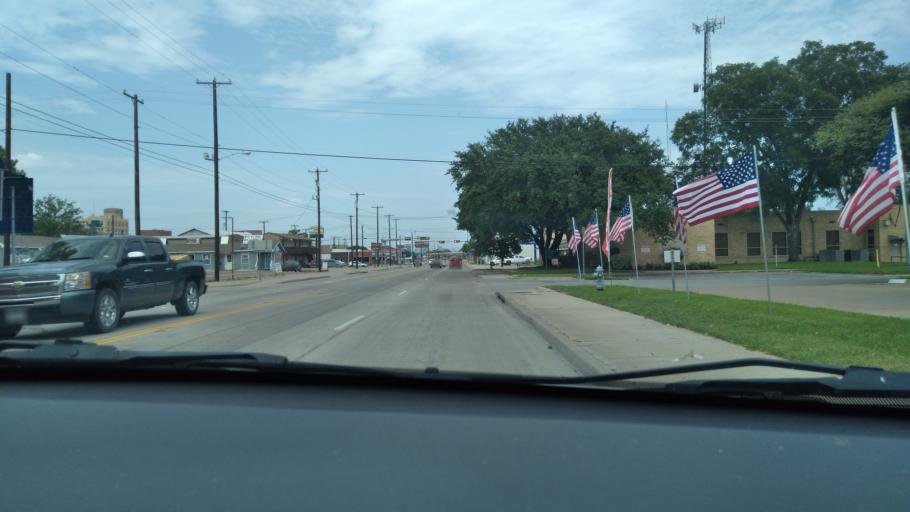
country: US
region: Texas
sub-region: Navarro County
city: Corsicana
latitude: 32.0902
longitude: -96.4662
